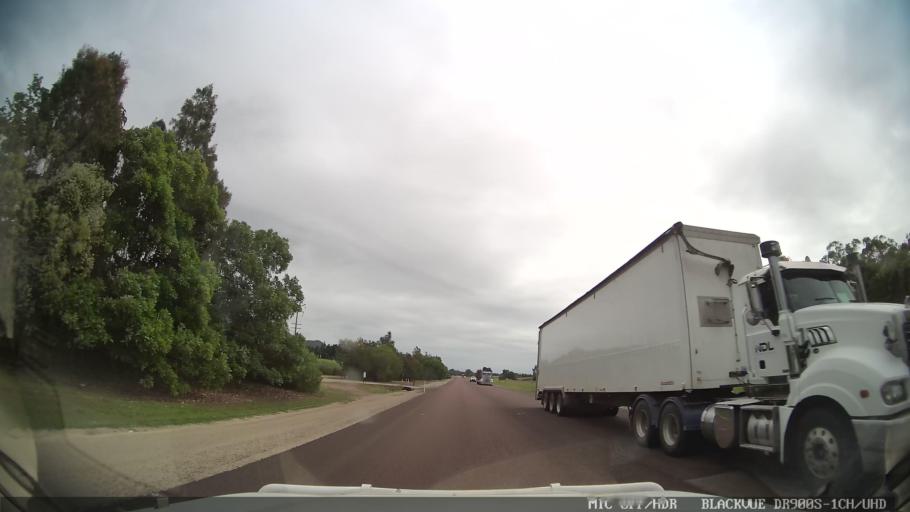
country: AU
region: Queensland
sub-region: Hinchinbrook
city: Ingham
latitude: -18.9260
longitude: 146.2629
